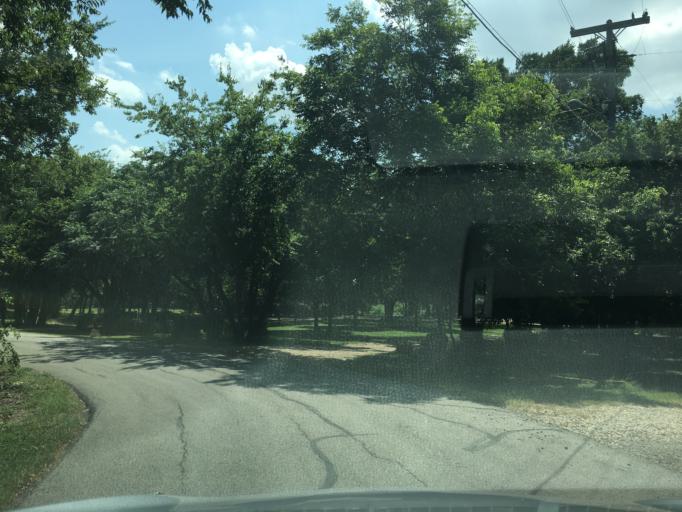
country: US
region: Texas
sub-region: Dallas County
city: Farmers Branch
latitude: 32.9228
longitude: -96.8658
